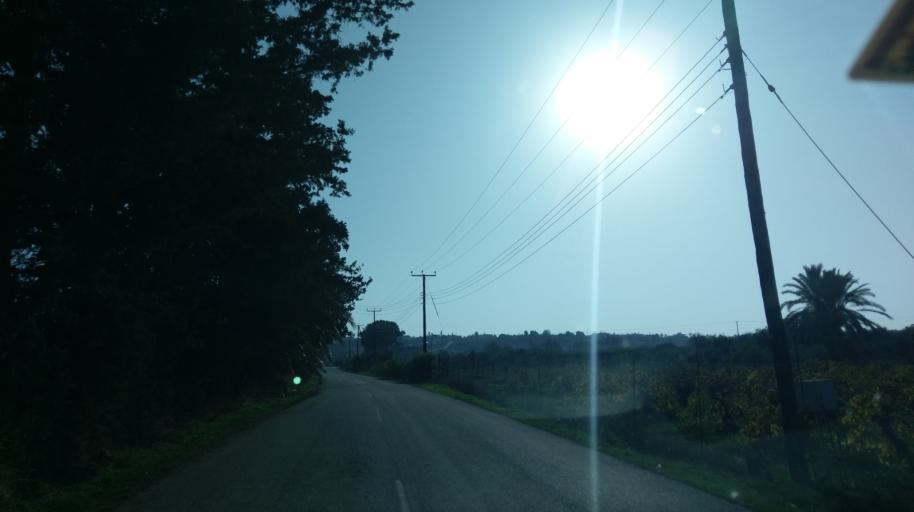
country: CY
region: Ammochostos
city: Leonarisso
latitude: 35.4323
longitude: 34.0794
